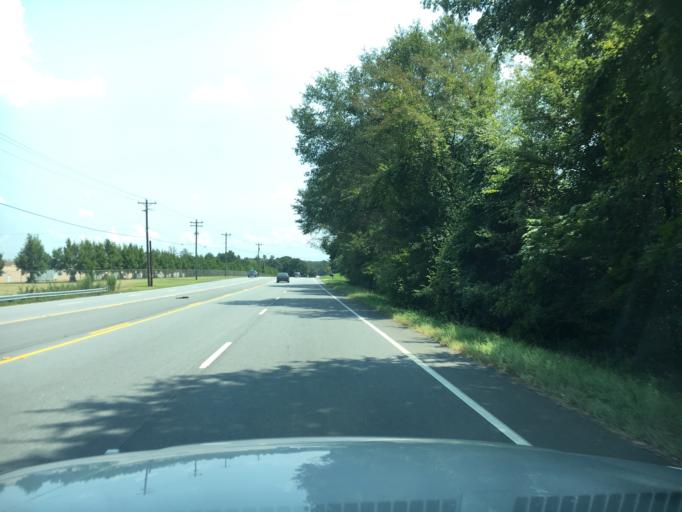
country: US
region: South Carolina
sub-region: Anderson County
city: Pendleton
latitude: 34.6136
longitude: -82.7704
